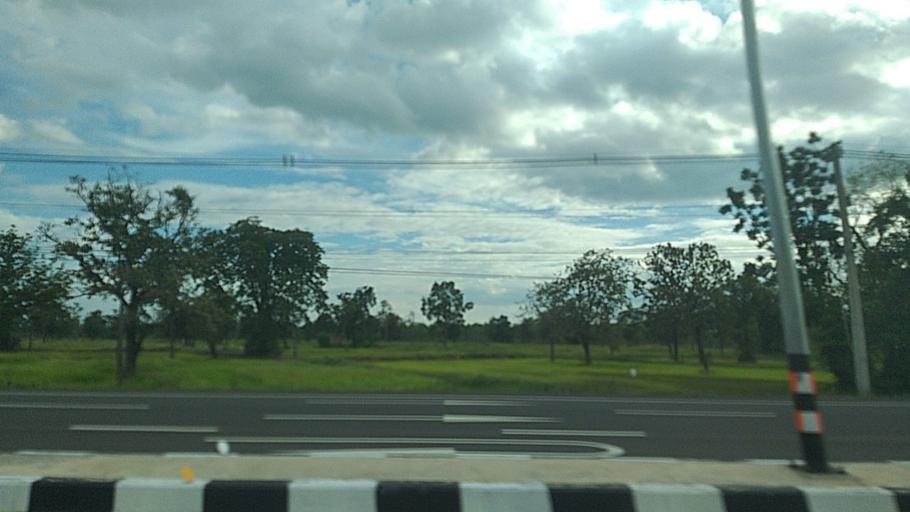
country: TH
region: Surin
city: Prasat
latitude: 14.5590
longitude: 103.5006
